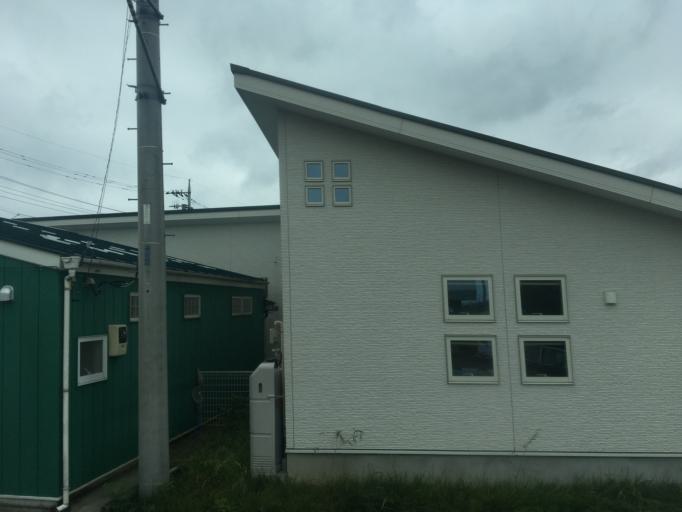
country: JP
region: Saitama
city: Kawagoe
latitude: 35.9294
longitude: 139.4933
